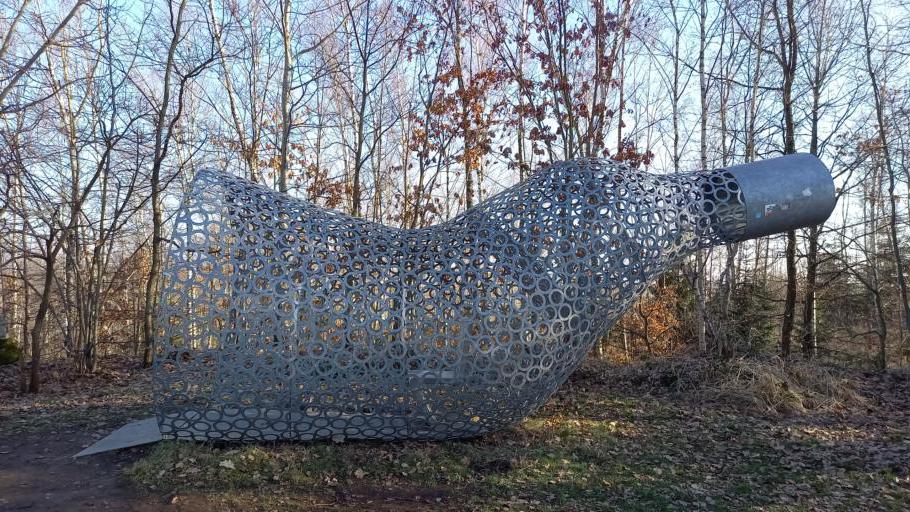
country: DE
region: Saxony
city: Oelsnitz
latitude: 50.7263
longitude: 12.6882
